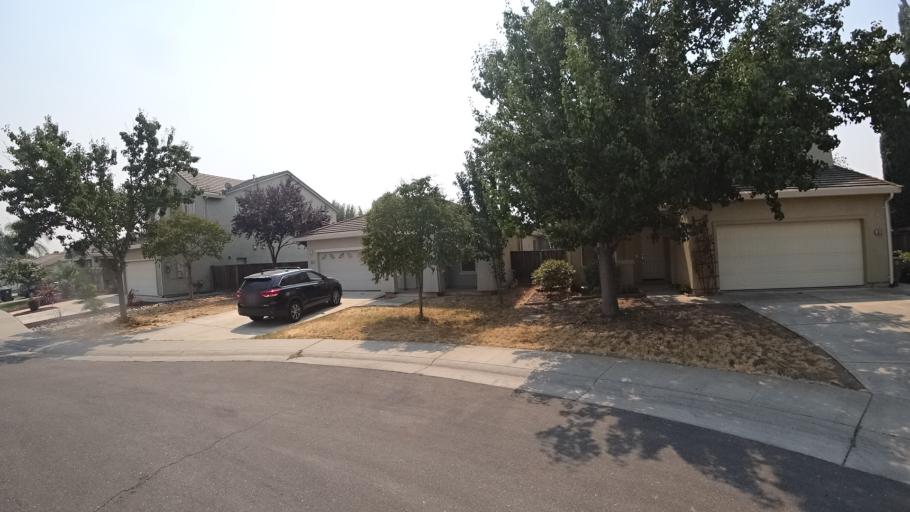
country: US
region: California
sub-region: Sacramento County
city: Laguna
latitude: 38.4025
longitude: -121.4360
